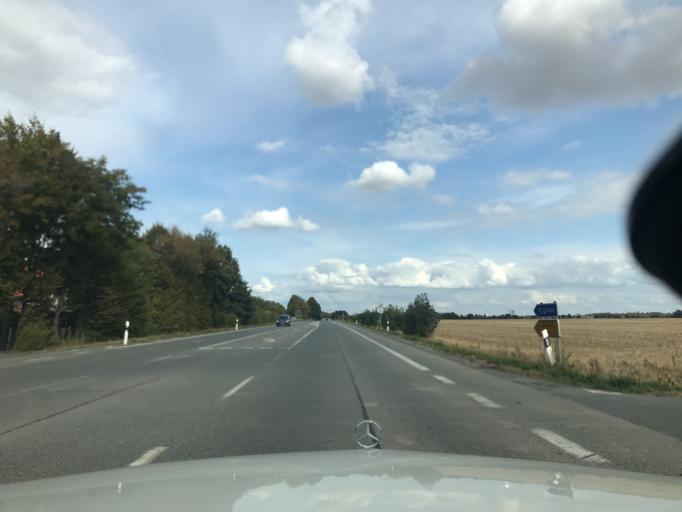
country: DE
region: North Rhine-Westphalia
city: Geseke
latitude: 51.6336
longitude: 8.4716
